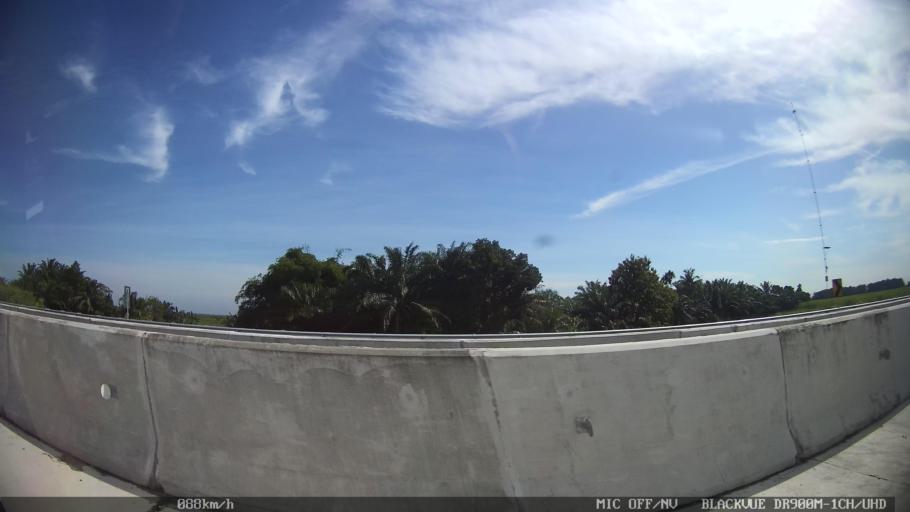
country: ID
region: North Sumatra
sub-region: Kabupaten Langkat
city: Stabat
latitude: 3.7110
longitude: 98.5312
